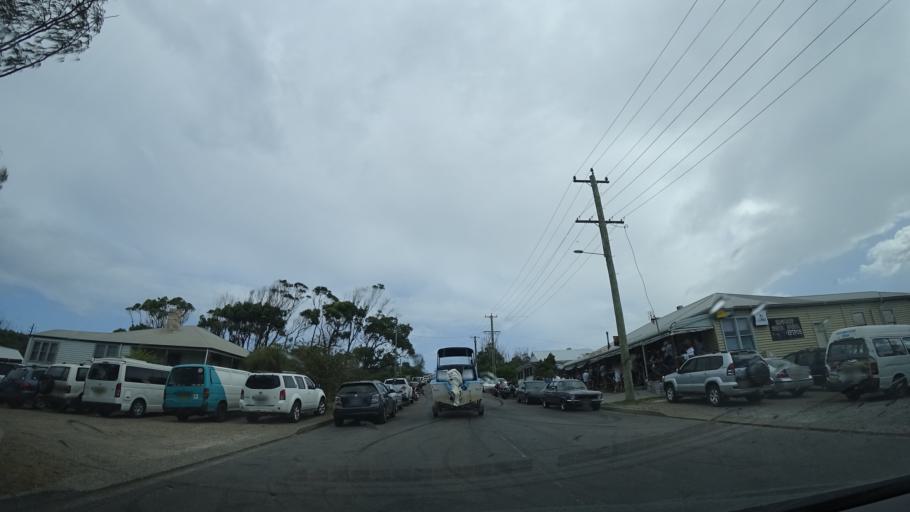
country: AU
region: New South Wales
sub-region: Wyong Shire
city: Kingfisher Shores
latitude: -33.1597
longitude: 151.6271
